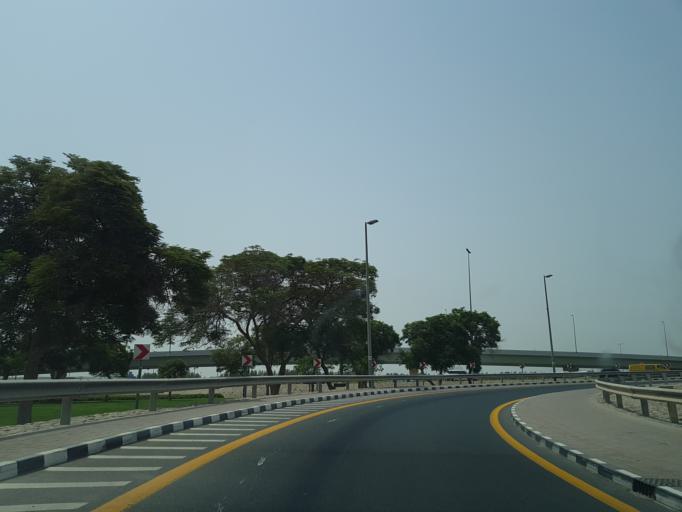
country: AE
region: Ash Shariqah
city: Sharjah
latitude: 25.2351
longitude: 55.3063
